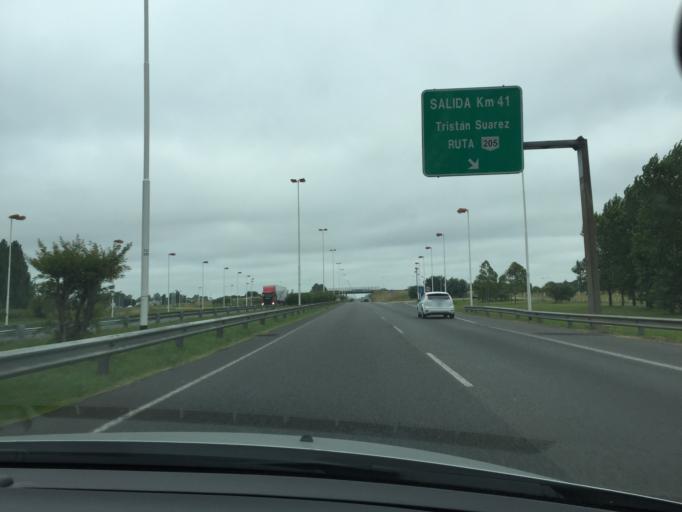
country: AR
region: Buenos Aires
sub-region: Partido de Ezeiza
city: Ezeiza
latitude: -34.8734
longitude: -58.5834
